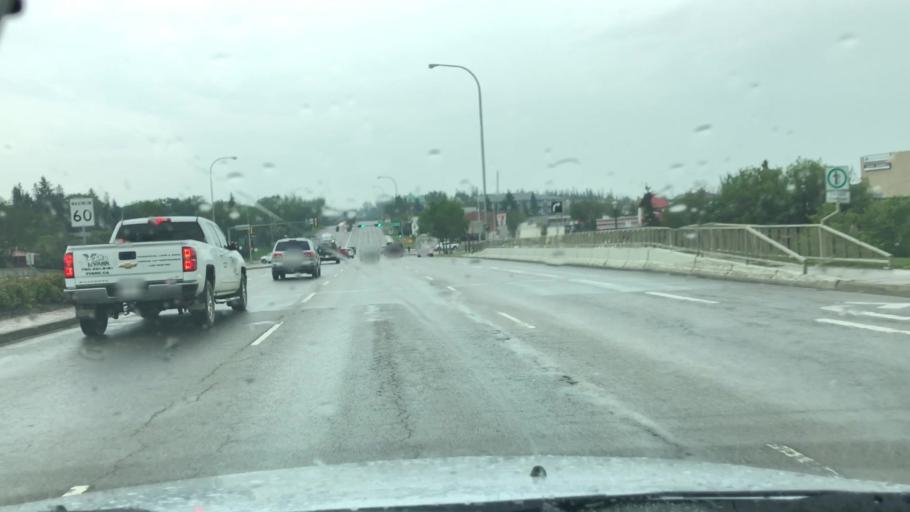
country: CA
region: Alberta
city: St. Albert
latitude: 53.6372
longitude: -113.6241
